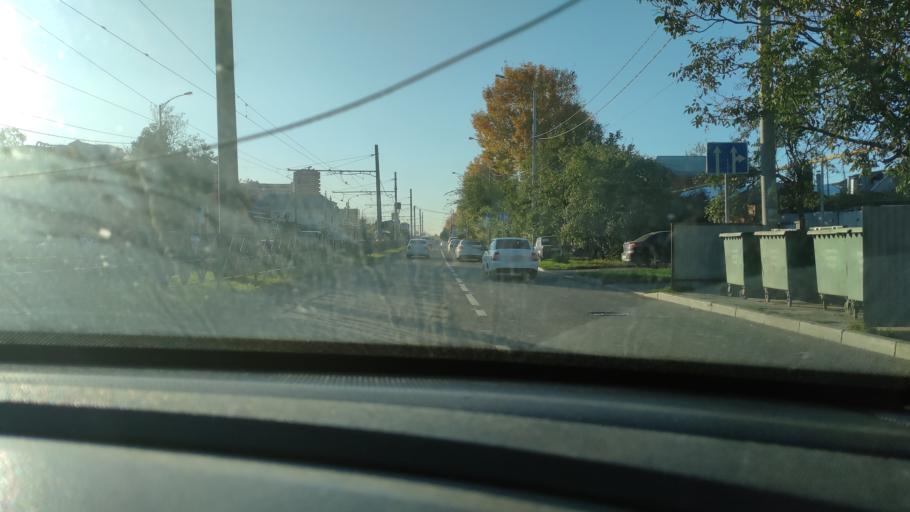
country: RU
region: Krasnodarskiy
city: Krasnodar
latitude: 45.0396
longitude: 38.9591
